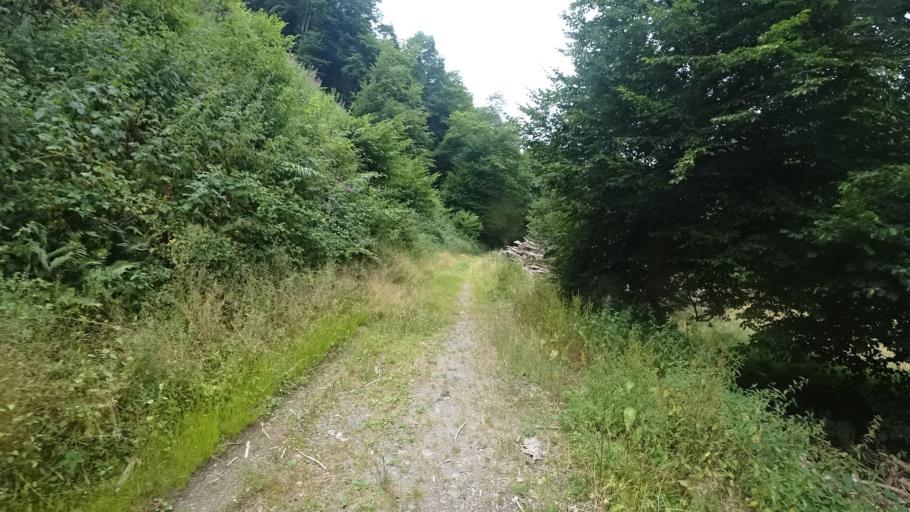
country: DE
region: Rheinland-Pfalz
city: Kesseling
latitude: 50.4830
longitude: 7.0132
